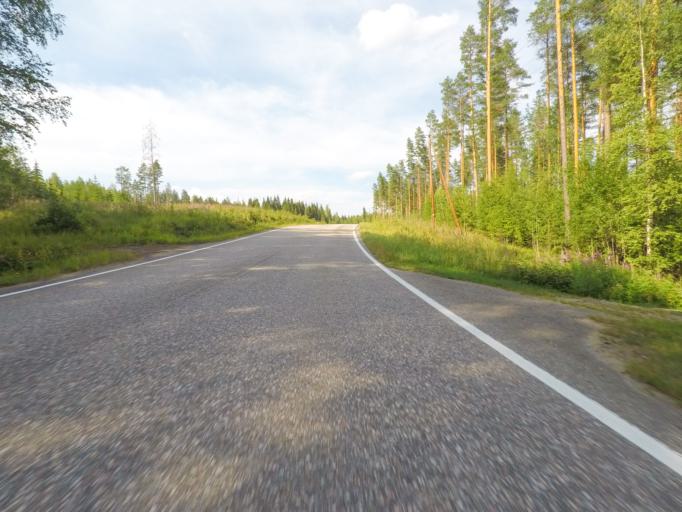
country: FI
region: Southern Savonia
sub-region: Savonlinna
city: Sulkava
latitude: 61.7750
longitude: 28.2391
